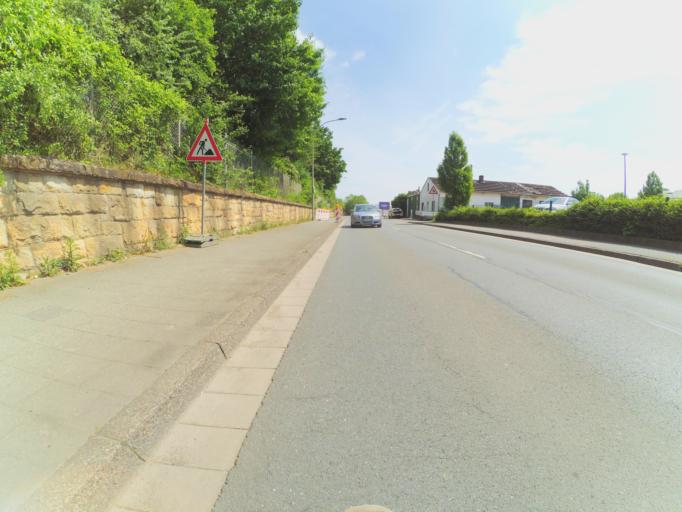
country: DE
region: North Rhine-Westphalia
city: Ibbenburen
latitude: 52.2767
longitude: 7.7230
